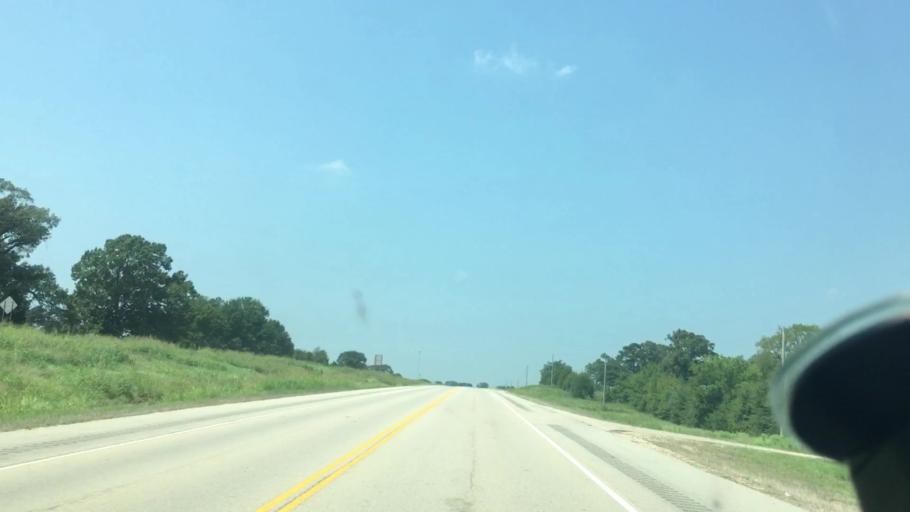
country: US
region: Oklahoma
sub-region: Atoka County
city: Atoka
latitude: 34.2880
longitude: -95.9619
